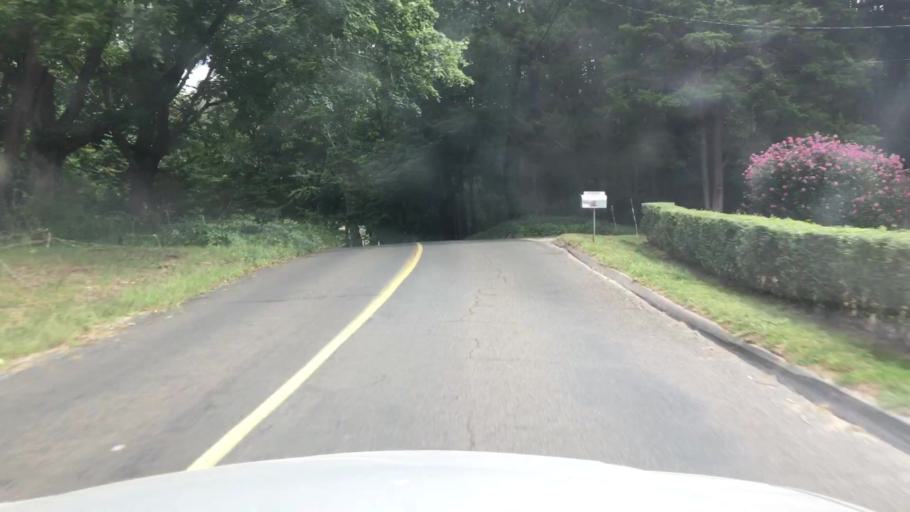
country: US
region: Connecticut
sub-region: Middlesex County
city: Essex Village
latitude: 41.3377
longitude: -72.3937
